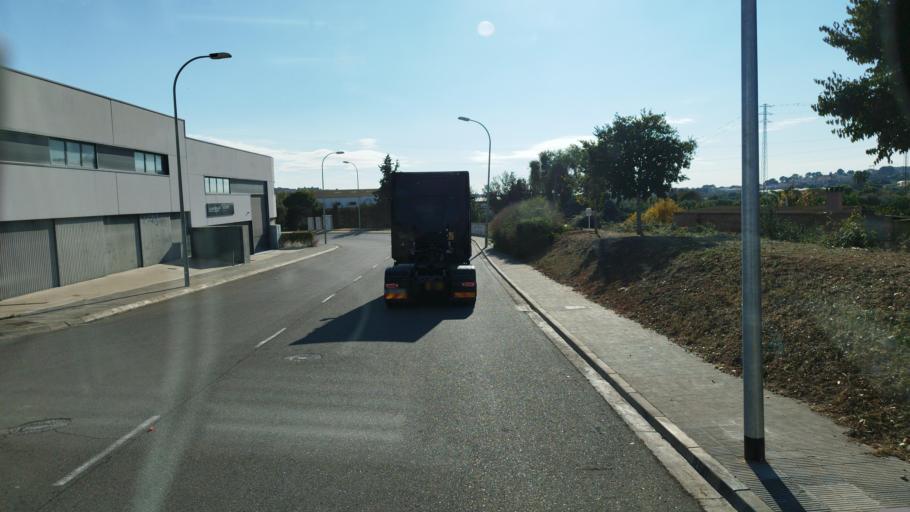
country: ES
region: Catalonia
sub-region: Provincia de Tarragona
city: Torredembarra
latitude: 41.1506
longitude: 1.3899
